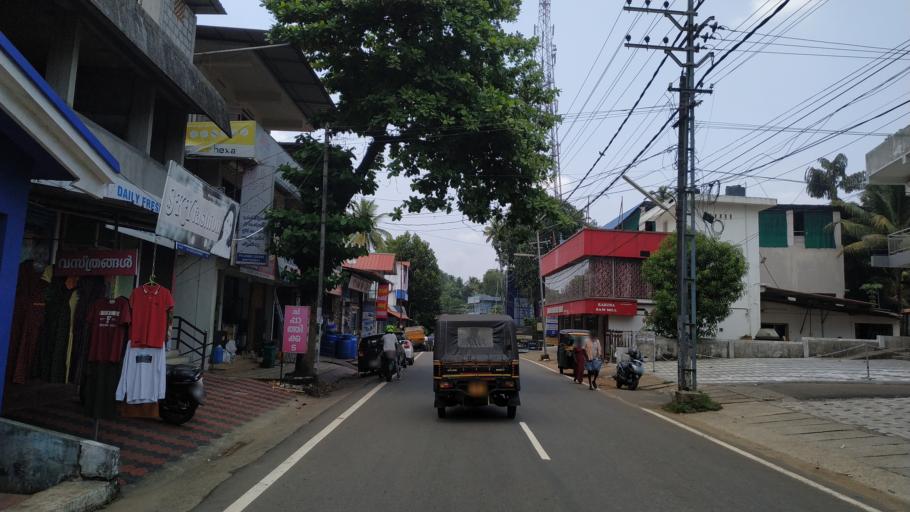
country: IN
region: Kerala
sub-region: Kottayam
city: Lalam
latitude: 9.8404
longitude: 76.7455
